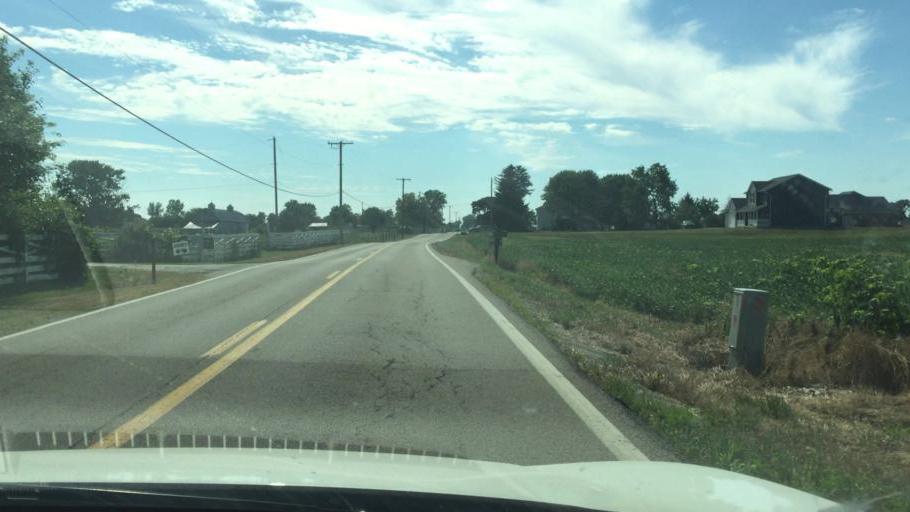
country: US
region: Ohio
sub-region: Clark County
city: Lisbon
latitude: 39.9413
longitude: -83.6545
